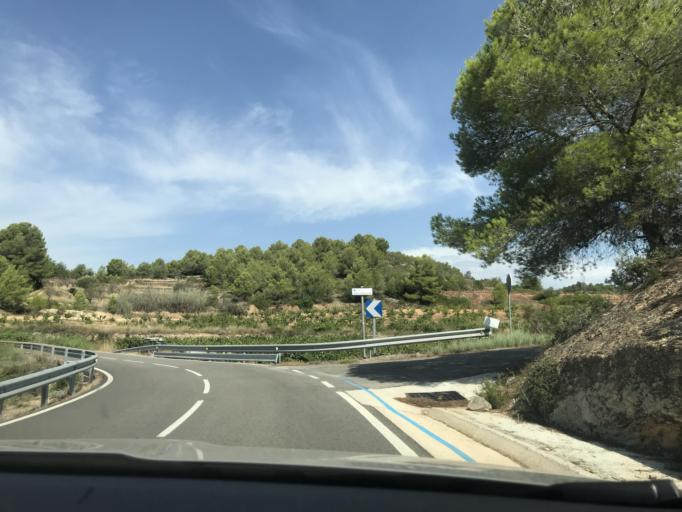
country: ES
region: Catalonia
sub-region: Provincia de Tarragona
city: Salomo
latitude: 41.2150
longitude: 1.3832
